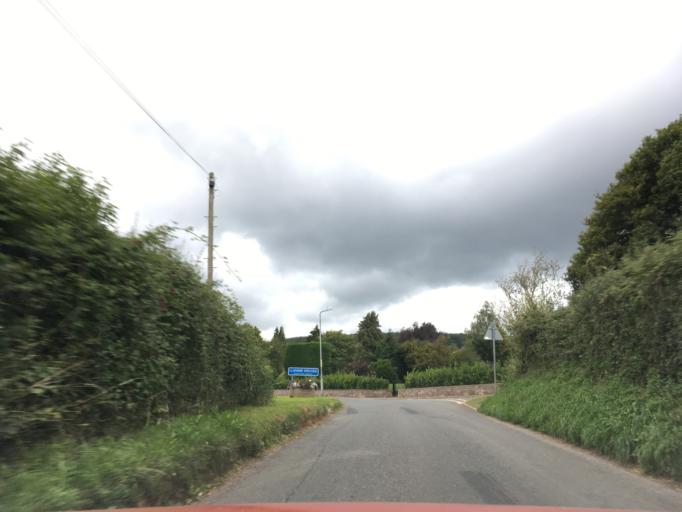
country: GB
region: Wales
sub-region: Newport
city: Llanvaches
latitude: 51.6263
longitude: -2.7951
